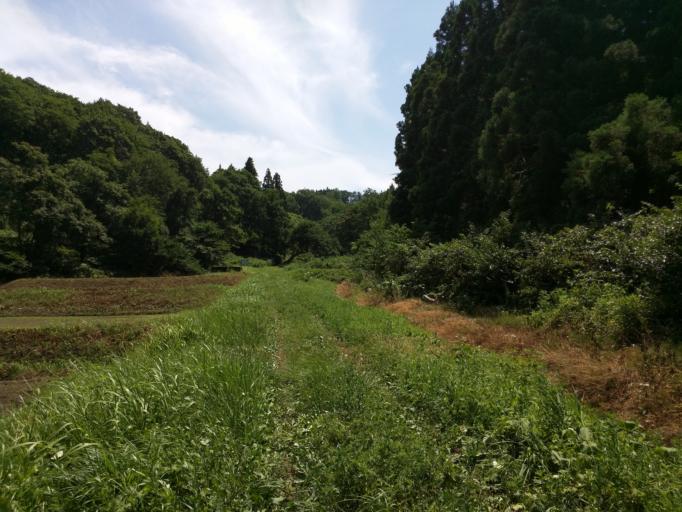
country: JP
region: Fukushima
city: Inawashiro
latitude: 37.5070
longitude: 139.9908
